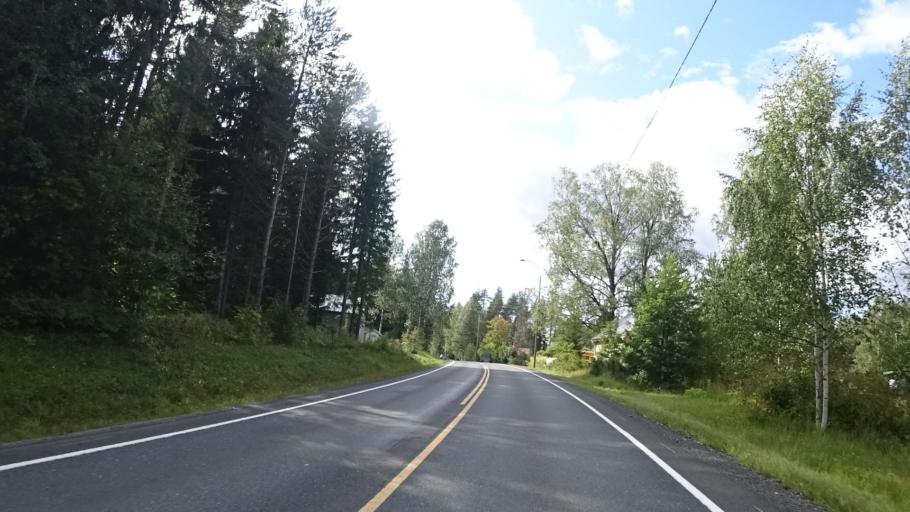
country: FI
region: North Karelia
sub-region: Keski-Karjala
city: Tohmajaervi
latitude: 62.1898
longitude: 30.4555
